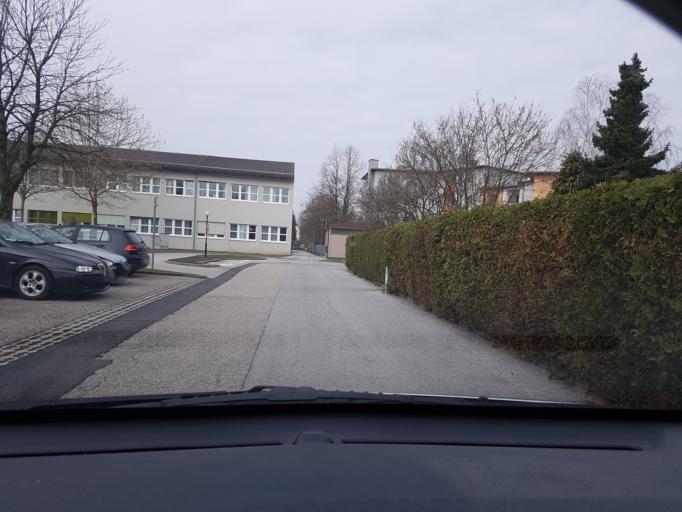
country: AT
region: Upper Austria
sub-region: Politischer Bezirk Linz-Land
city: Asten
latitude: 48.2210
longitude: 14.4210
